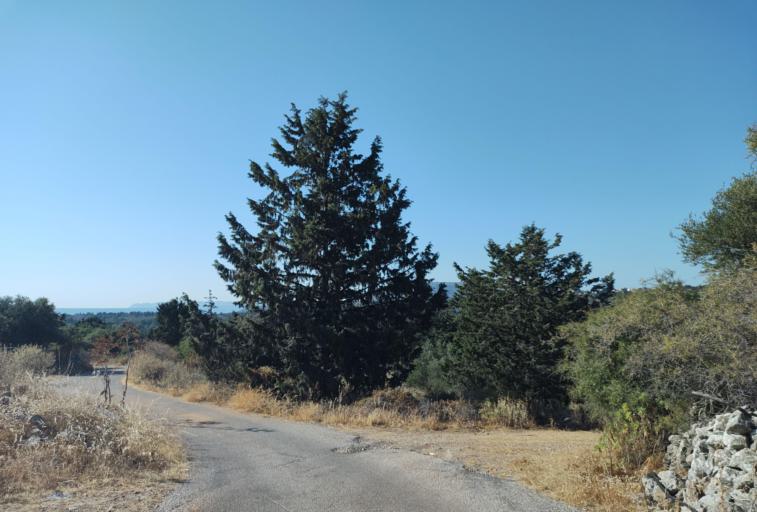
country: GR
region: Crete
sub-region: Nomos Chanias
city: Georgioupolis
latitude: 35.3957
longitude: 24.2370
